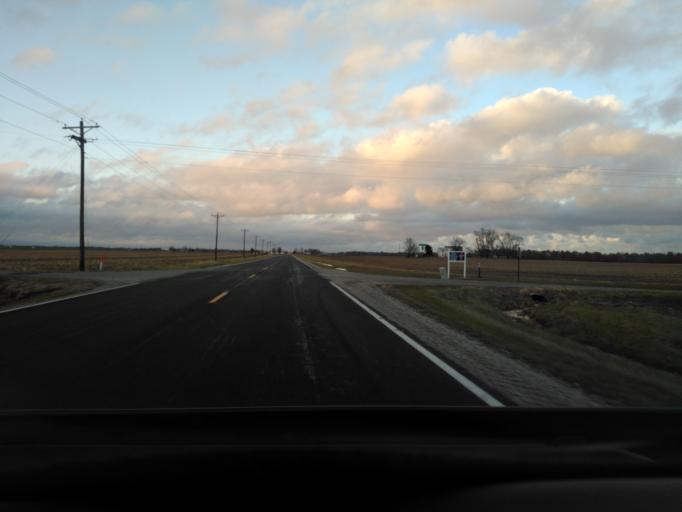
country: US
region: Illinois
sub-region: Effingham County
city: Altamont
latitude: 39.0006
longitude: -88.7486
